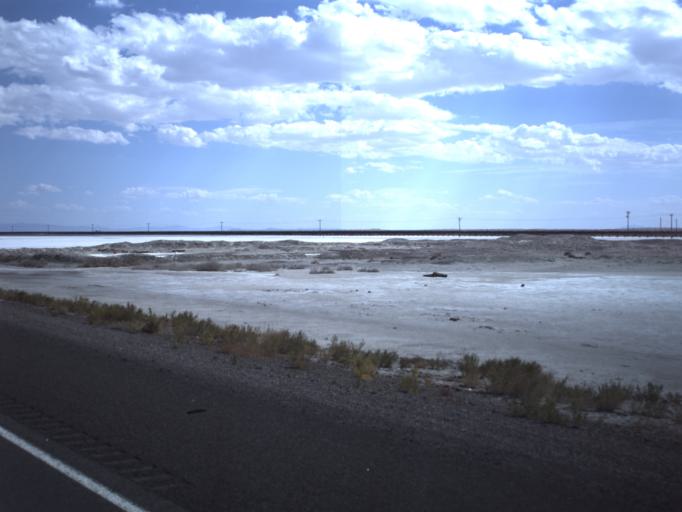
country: US
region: Utah
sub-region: Tooele County
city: Wendover
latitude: 40.7372
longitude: -113.7903
